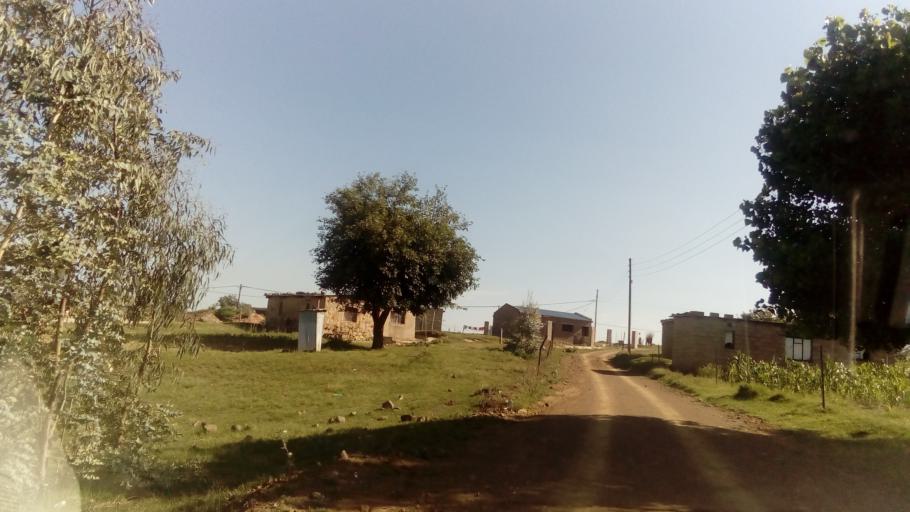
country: LS
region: Berea
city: Teyateyaneng
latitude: -29.1386
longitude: 27.7487
